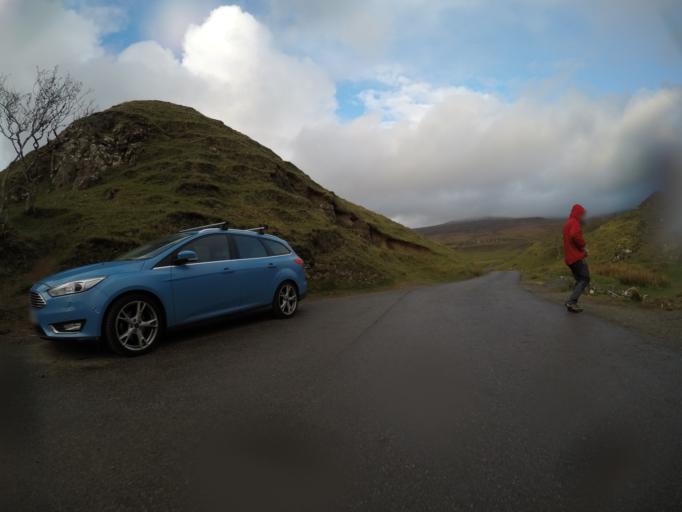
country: GB
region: Scotland
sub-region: Highland
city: Portree
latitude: 57.5837
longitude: -6.3250
